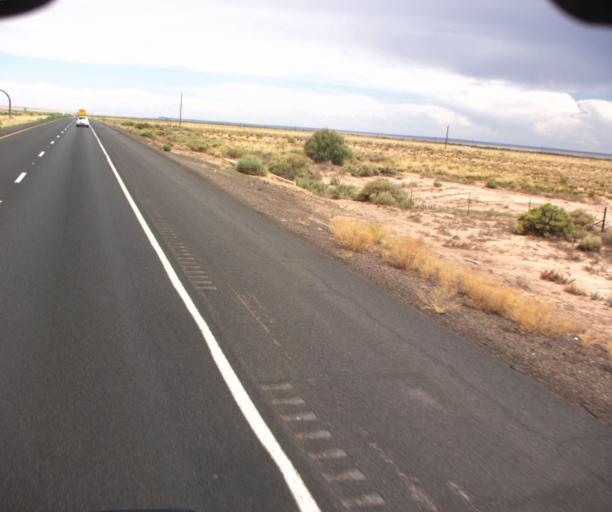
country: US
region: Arizona
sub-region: Navajo County
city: Winslow
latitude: 35.0009
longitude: -110.6013
